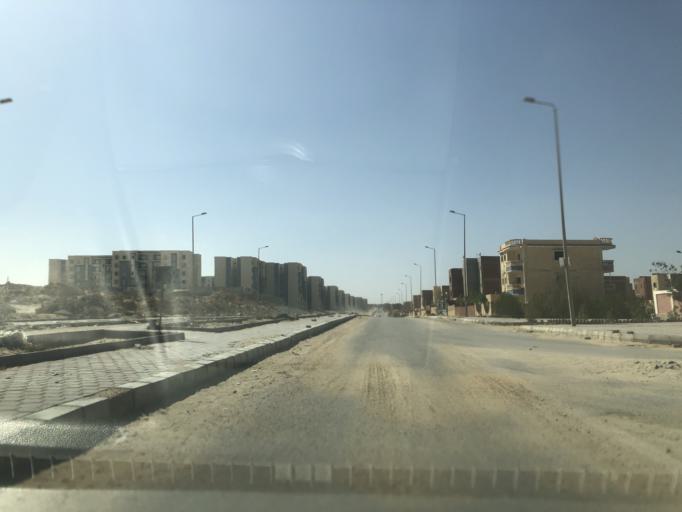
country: EG
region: Al Jizah
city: Madinat Sittah Uktubar
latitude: 29.9280
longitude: 30.9931
